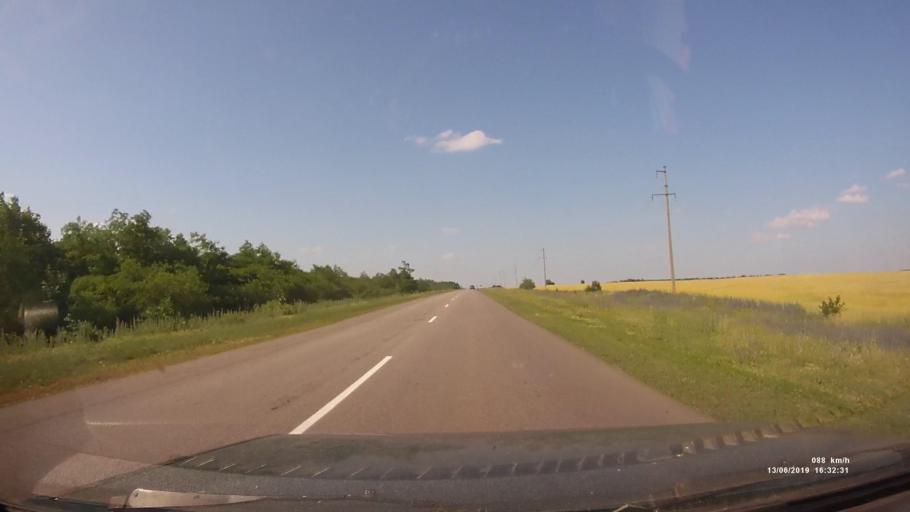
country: RU
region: Rostov
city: Kazanskaya
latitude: 49.8492
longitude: 41.2718
